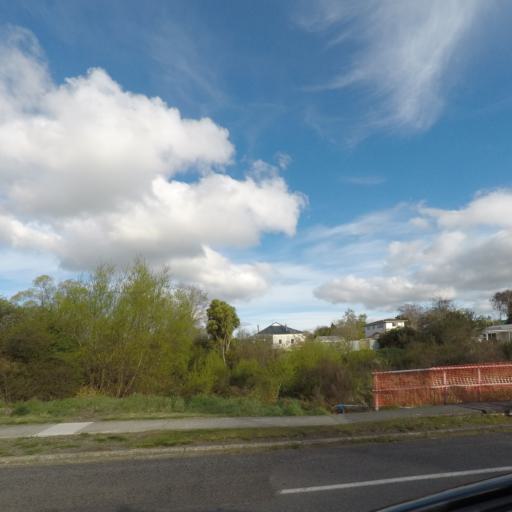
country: NZ
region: Manawatu-Wanganui
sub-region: Ruapehu District
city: Waiouru
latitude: -39.4133
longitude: 175.4035
